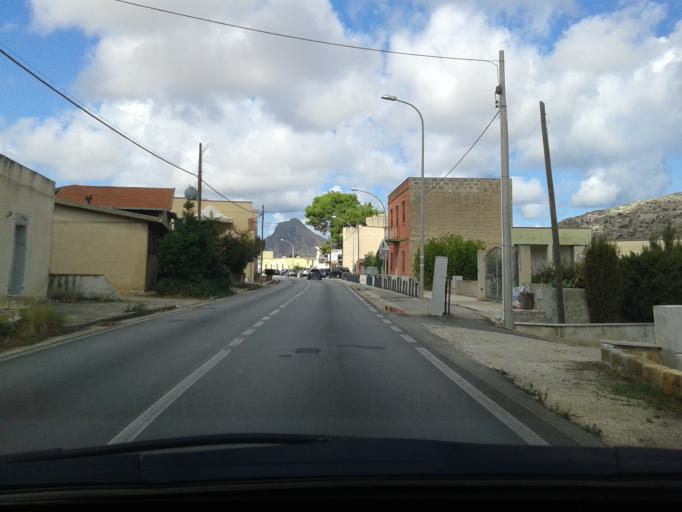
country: IT
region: Sicily
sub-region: Trapani
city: Castelluzzo
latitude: 38.0798
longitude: 12.7174
